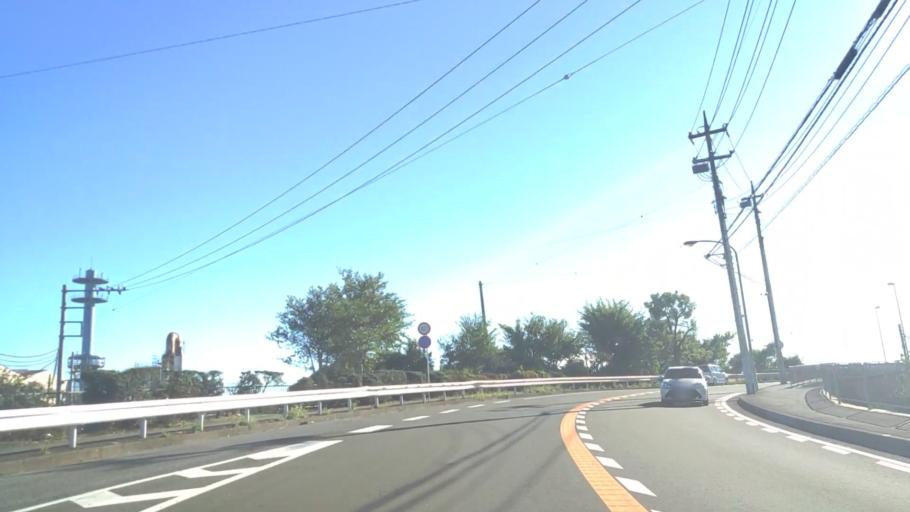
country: JP
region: Kanagawa
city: Atsugi
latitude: 35.4540
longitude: 139.3693
